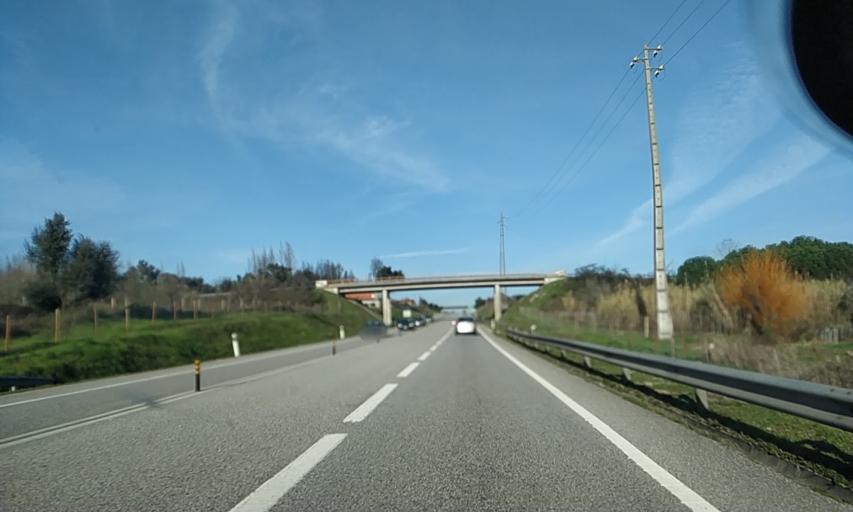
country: PT
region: Viseu
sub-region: Santa Comba Dao
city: Santa Comba Dao
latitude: 40.3668
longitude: -8.1313
